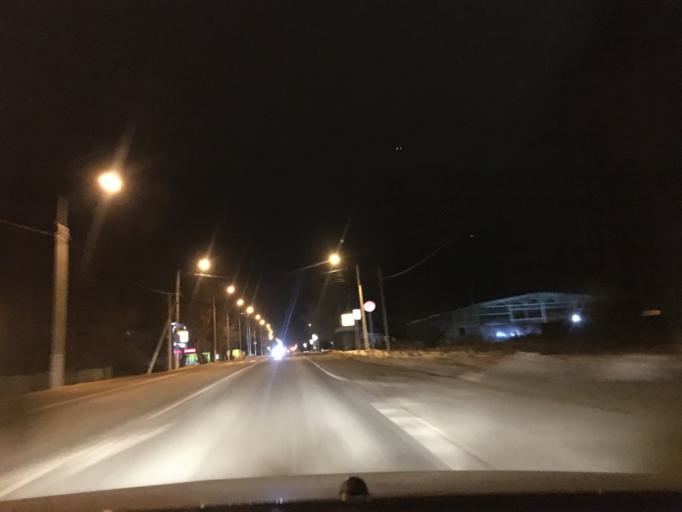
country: RU
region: Tula
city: Pervomayskiy
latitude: 54.0487
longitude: 37.5298
